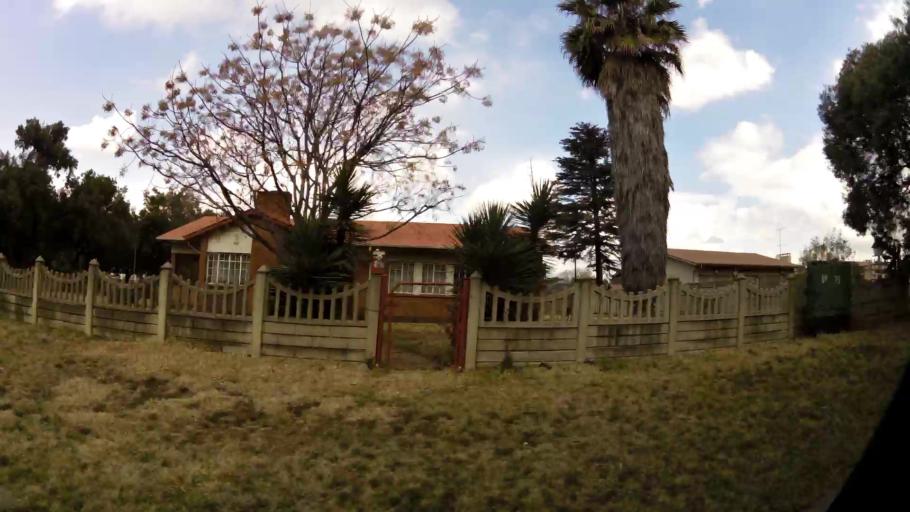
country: ZA
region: Gauteng
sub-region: Sedibeng District Municipality
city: Vanderbijlpark
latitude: -26.7113
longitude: 27.8396
